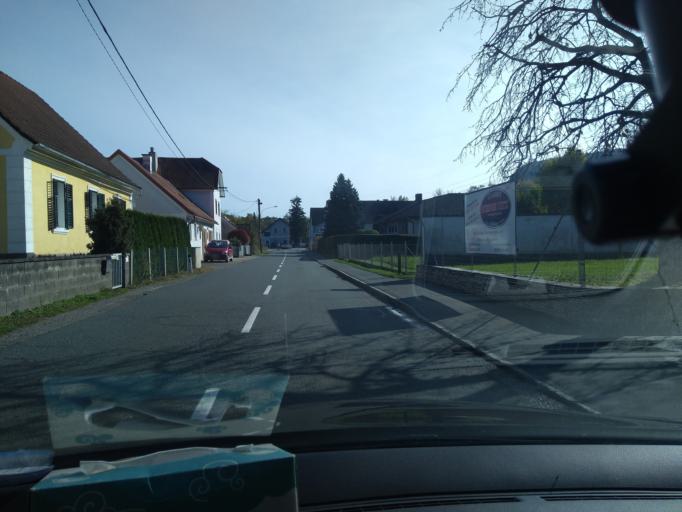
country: AT
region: Styria
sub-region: Politischer Bezirk Leibnitz
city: Wildon
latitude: 46.8882
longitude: 15.5195
